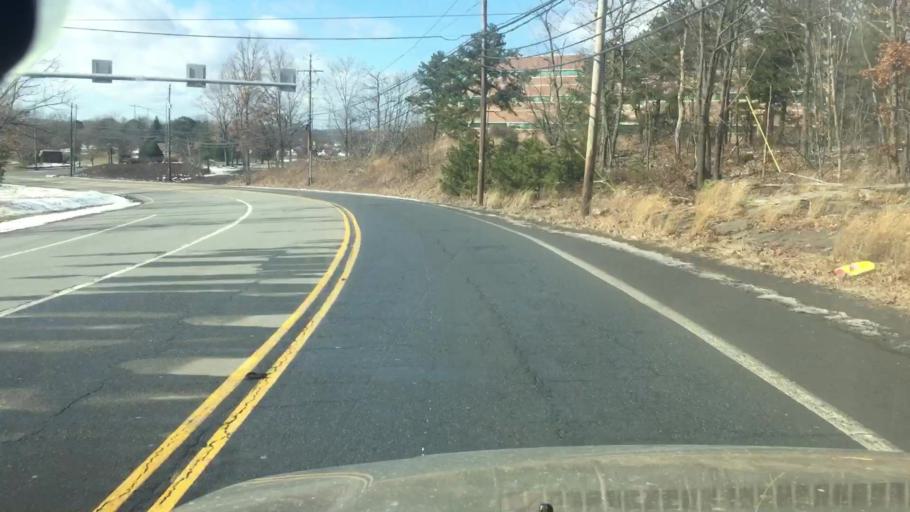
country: US
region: Pennsylvania
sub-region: Luzerne County
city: Hudson
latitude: 41.2515
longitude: -75.8092
